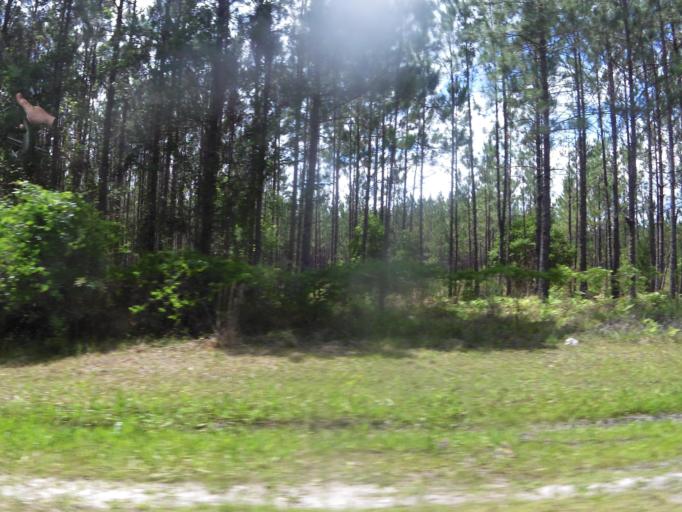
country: US
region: Florida
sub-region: Clay County
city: Green Cove Springs
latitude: 29.9338
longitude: -81.7511
